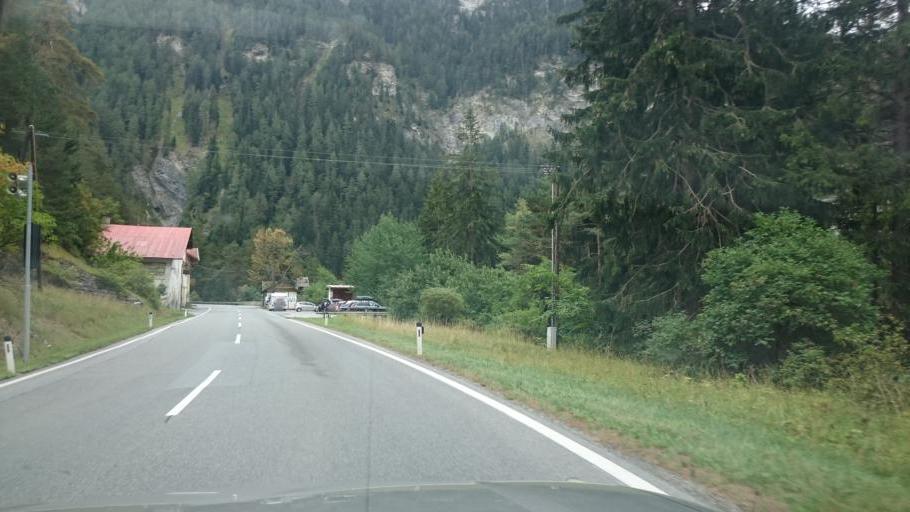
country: AT
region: Tyrol
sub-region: Politischer Bezirk Landeck
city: Nauders
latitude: 46.9306
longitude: 10.4887
